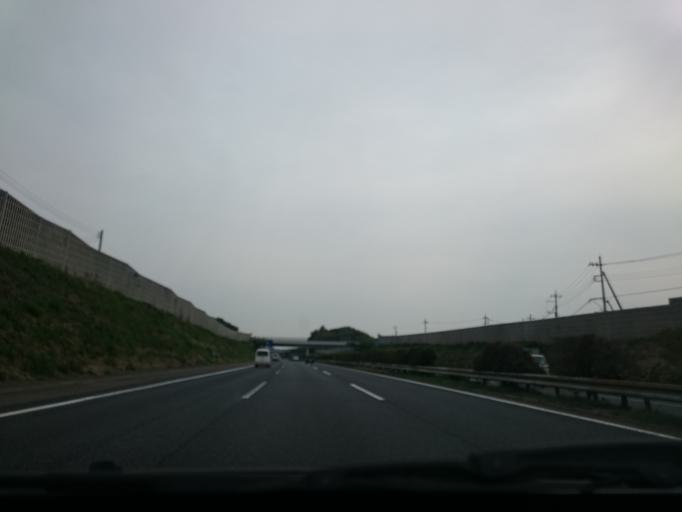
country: JP
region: Tochigi
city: Utsunomiya-shi
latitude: 36.5668
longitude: 139.8190
